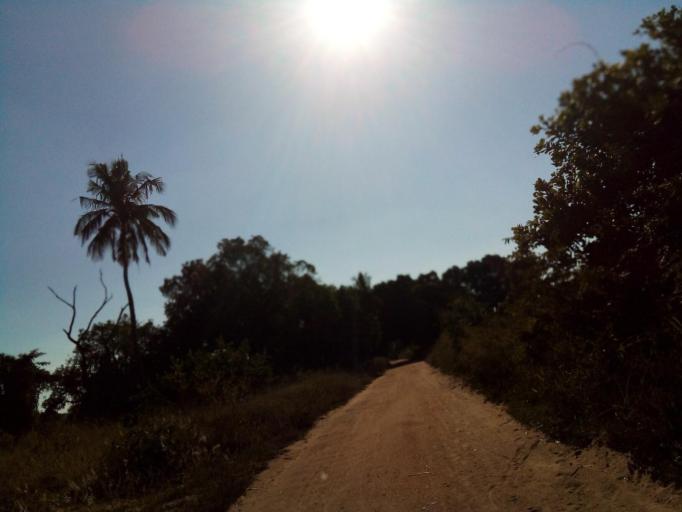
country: MZ
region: Zambezia
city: Quelimane
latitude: -17.5245
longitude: 36.6155
